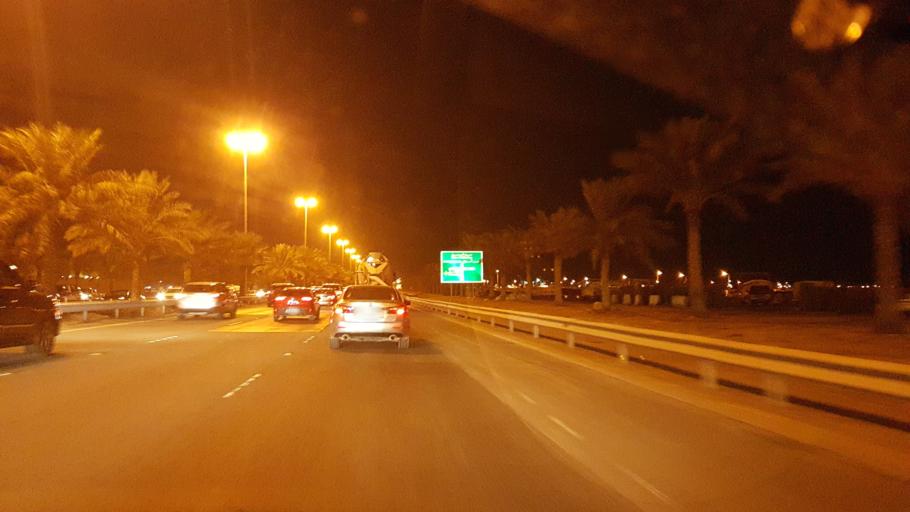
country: BH
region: Muharraq
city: Al Hadd
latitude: 26.2459
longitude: 50.6586
